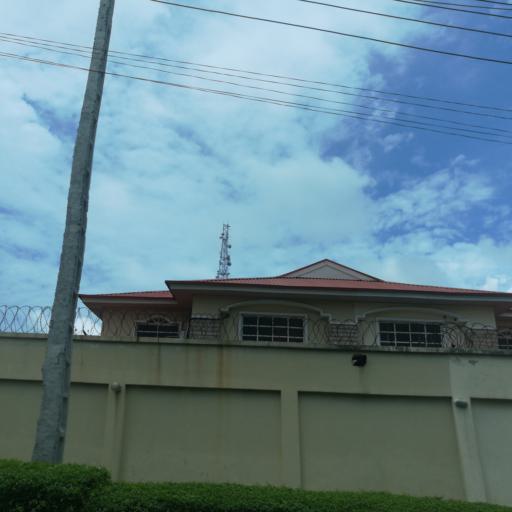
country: NG
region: Lagos
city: Ikoyi
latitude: 6.4419
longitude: 3.4650
